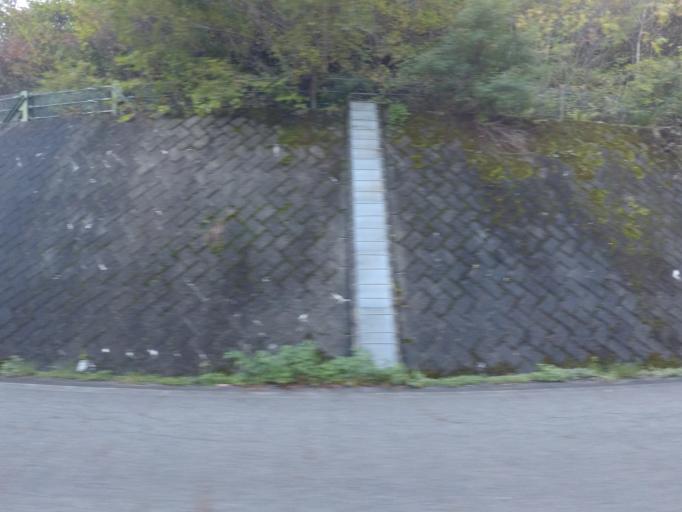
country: JP
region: Nagano
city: Tatsuno
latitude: 35.9806
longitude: 137.7667
